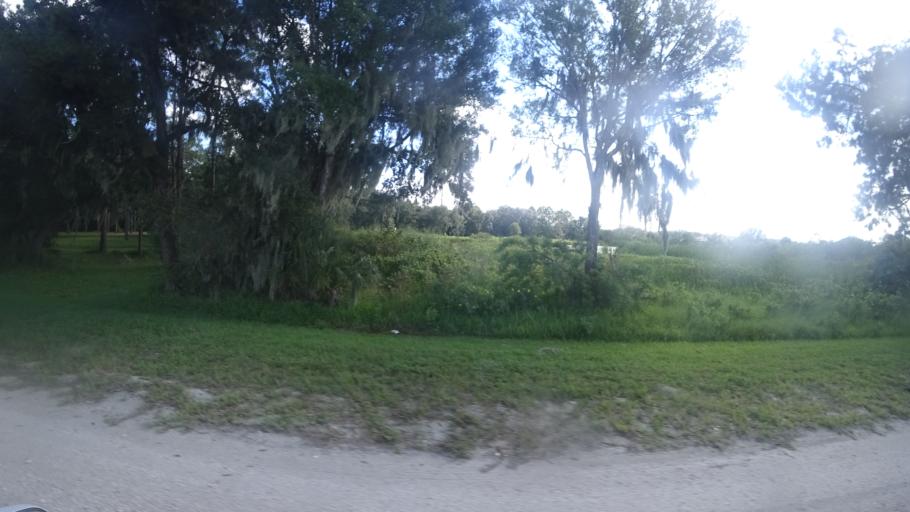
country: US
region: Florida
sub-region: Manatee County
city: Ellenton
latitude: 27.6277
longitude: -82.4974
